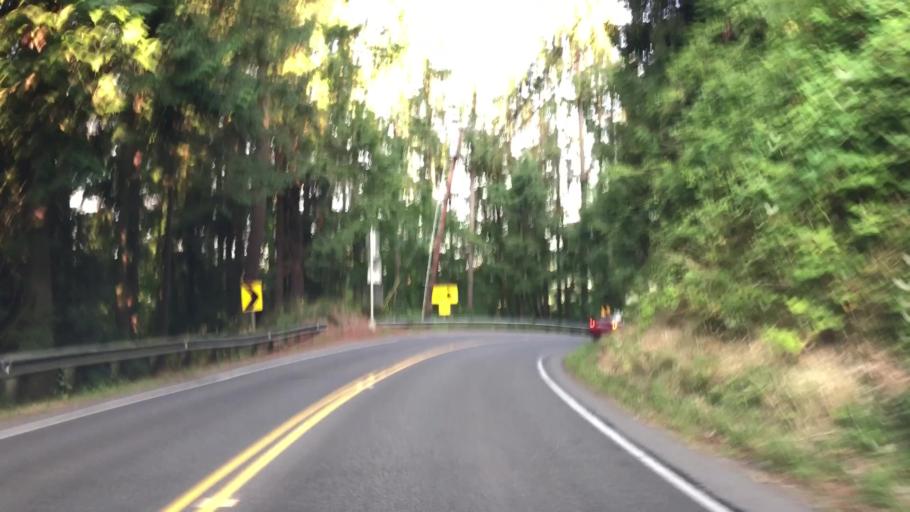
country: US
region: Washington
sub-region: King County
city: Sammamish
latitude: 47.6711
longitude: -122.0697
